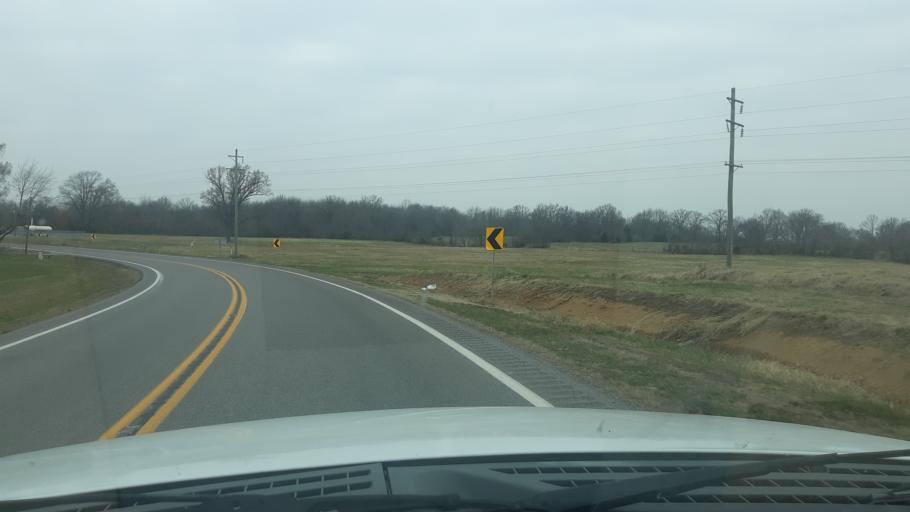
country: US
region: Illinois
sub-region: Saline County
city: Harrisburg
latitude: 37.8341
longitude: -88.5403
